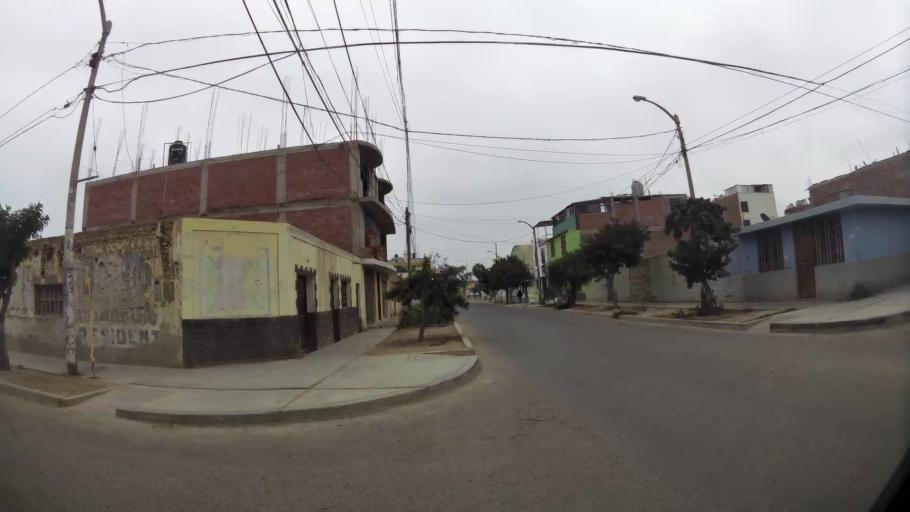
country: PE
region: La Libertad
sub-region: Provincia de Trujillo
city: Buenos Aires
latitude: -8.1395
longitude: -79.0472
